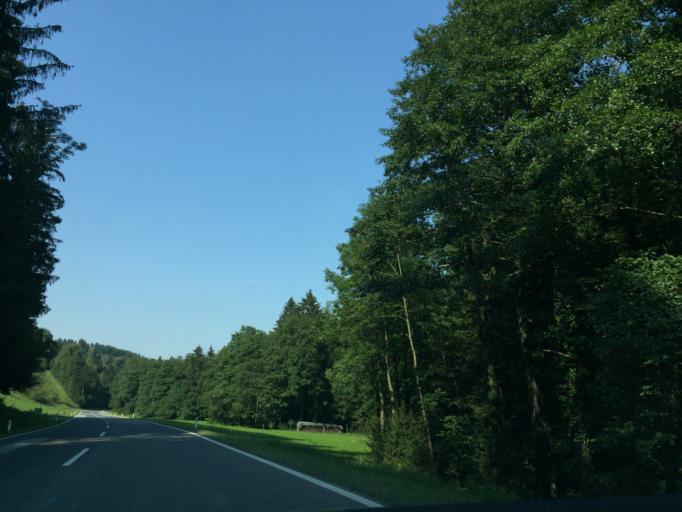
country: AT
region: Styria
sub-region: Politischer Bezirk Deutschlandsberg
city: Aibl
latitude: 46.6633
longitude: 15.2141
